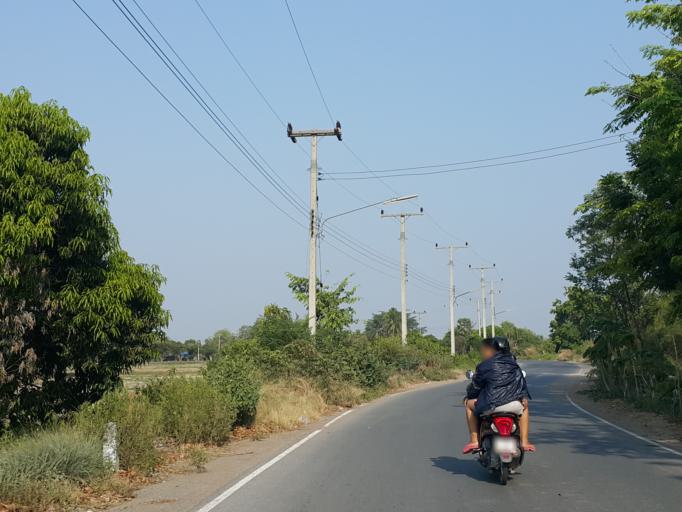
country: TH
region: Suphan Buri
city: Sam Chuk
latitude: 14.7454
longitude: 100.0344
